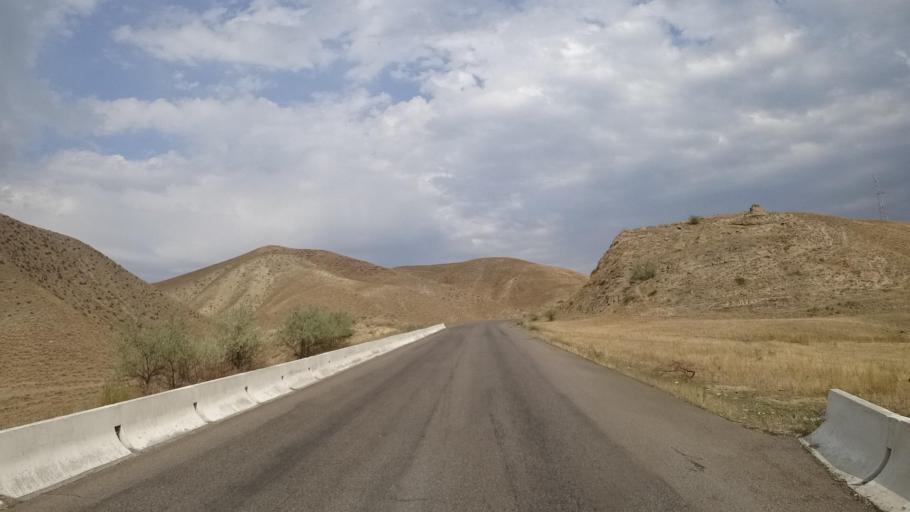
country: KG
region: Jalal-Abad
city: Toktogul
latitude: 41.7810
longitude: 72.9911
